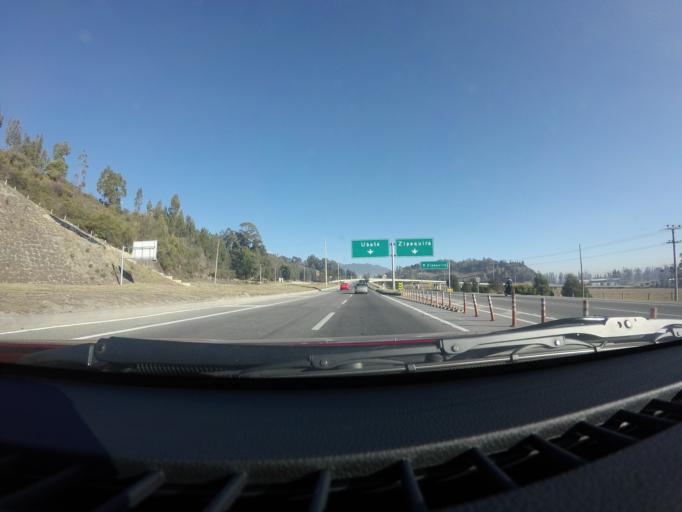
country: CO
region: Cundinamarca
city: Zipaquira
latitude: 4.9956
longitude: -74.0031
